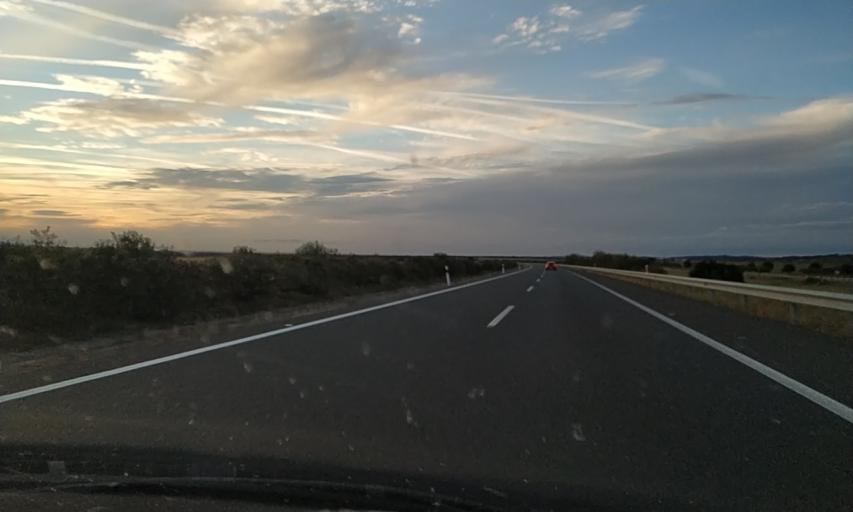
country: ES
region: Extremadura
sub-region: Provincia de Caceres
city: Casas de Don Antonio
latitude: 39.2498
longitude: -6.3076
